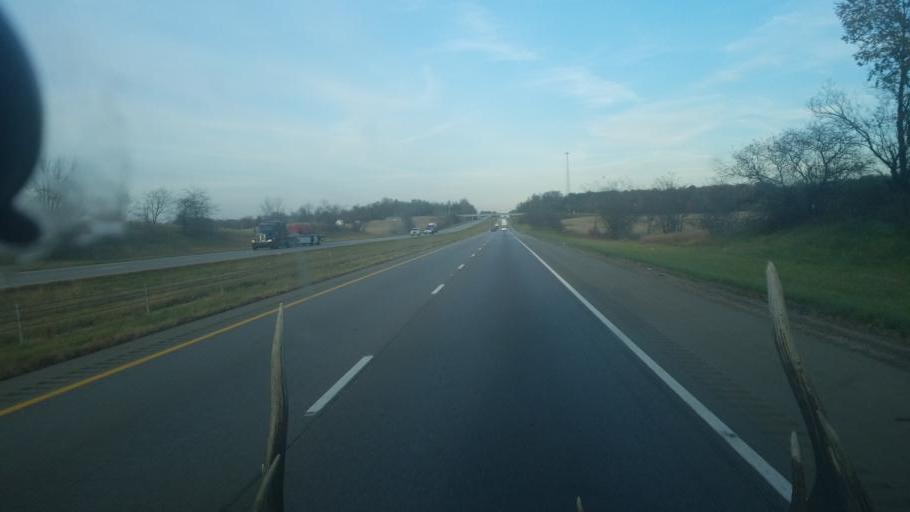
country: US
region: Ohio
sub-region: Perry County
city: Somerset
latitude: 39.9432
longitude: -82.2300
